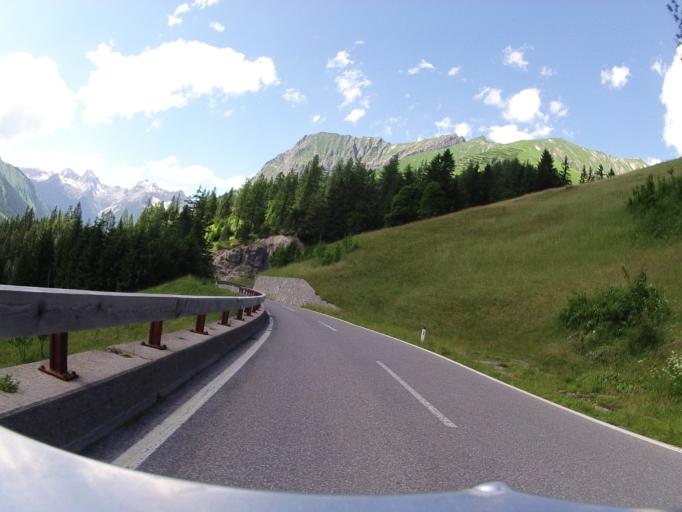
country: AT
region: Tyrol
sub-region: Politischer Bezirk Reutte
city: Elmen
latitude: 47.3059
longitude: 10.5904
